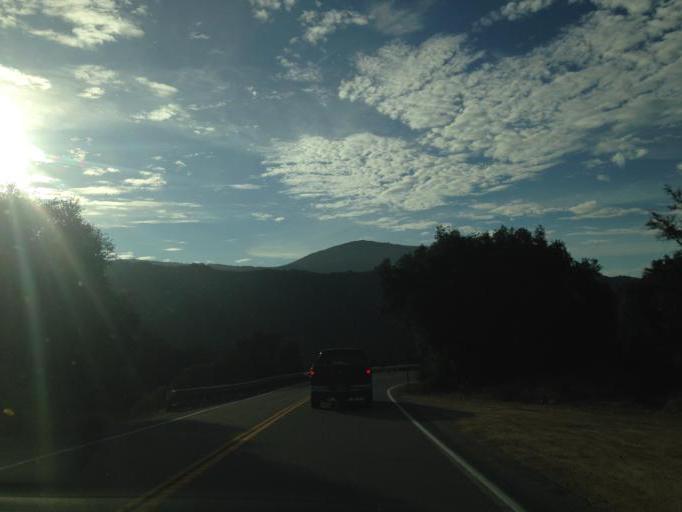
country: US
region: California
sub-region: San Diego County
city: Rainbow
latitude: 33.4067
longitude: -117.0836
